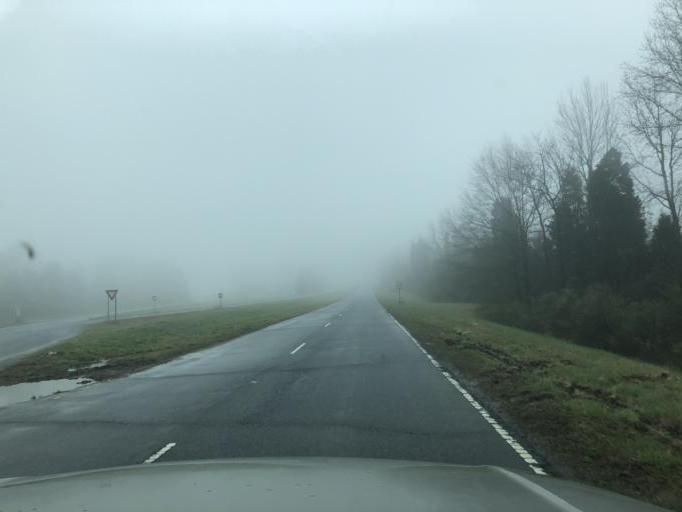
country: US
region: North Carolina
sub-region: Cleveland County
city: White Plains
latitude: 35.1947
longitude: -81.3993
